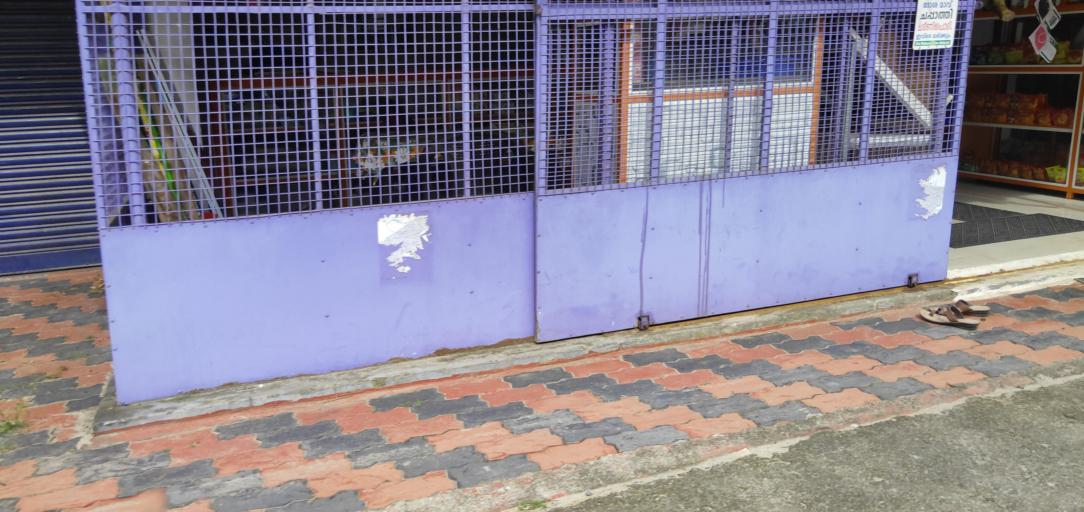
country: IN
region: Kerala
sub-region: Alappuzha
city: Kayankulam
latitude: 9.2290
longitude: 76.4580
